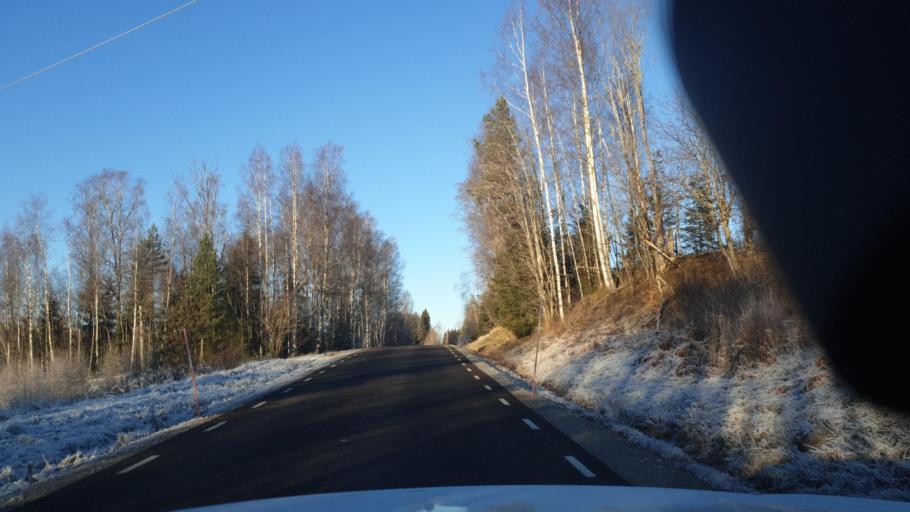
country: SE
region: Vaermland
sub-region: Sunne Kommun
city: Sunne
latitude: 59.6727
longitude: 12.9039
